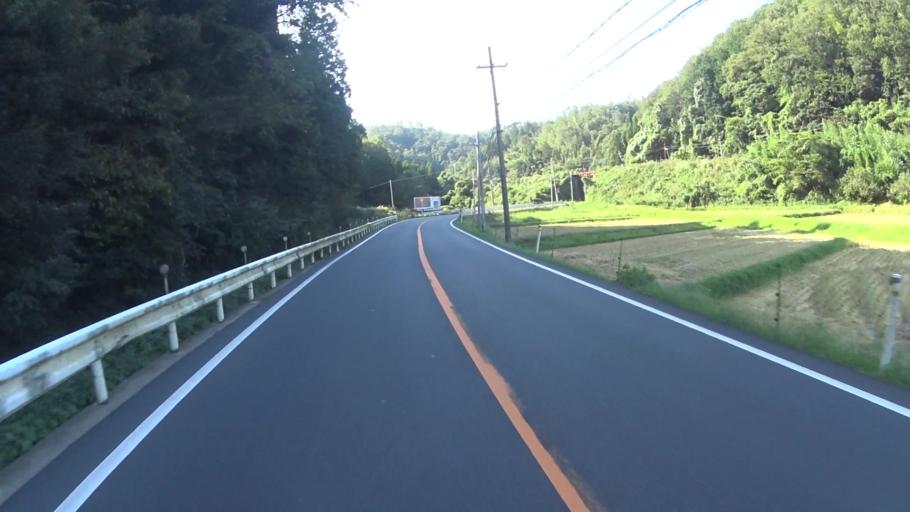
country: JP
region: Kyoto
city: Miyazu
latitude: 35.6606
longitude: 135.0185
